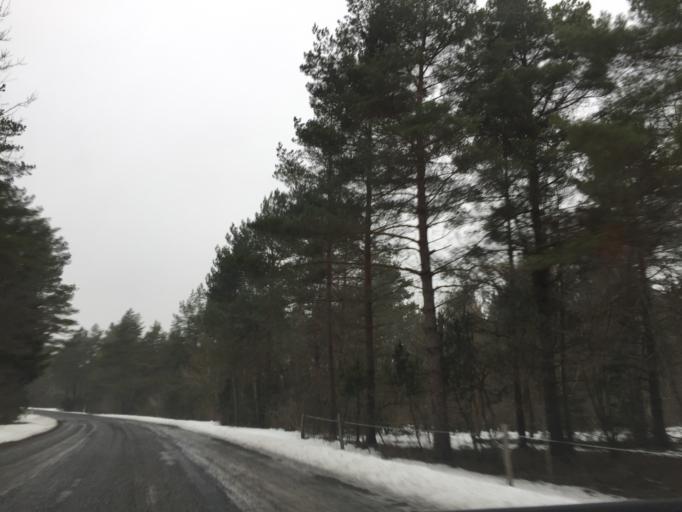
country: EE
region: Saare
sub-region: Orissaare vald
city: Orissaare
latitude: 58.3921
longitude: 22.8562
